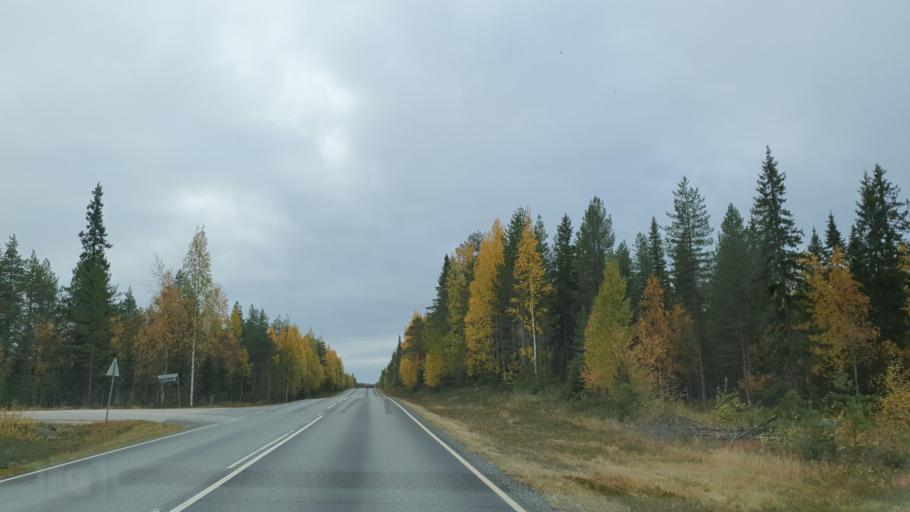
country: FI
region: Lapland
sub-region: Rovaniemi
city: Ranua
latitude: 65.7989
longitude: 26.5704
